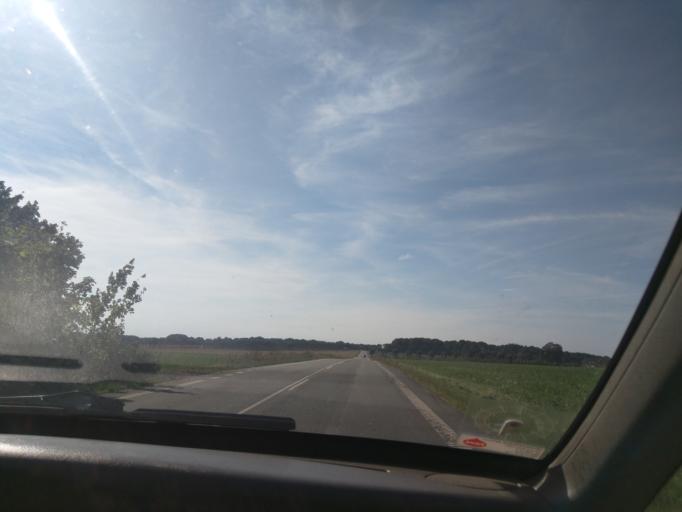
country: DK
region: Central Jutland
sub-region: Viborg Kommune
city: Bjerringbro
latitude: 56.4348
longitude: 9.6624
